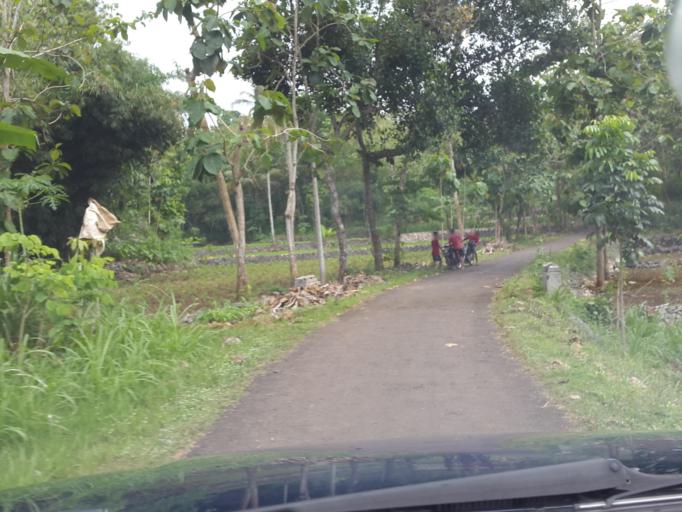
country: ID
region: Daerah Istimewa Yogyakarta
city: Pundong
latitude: -8.0390
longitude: 110.4670
